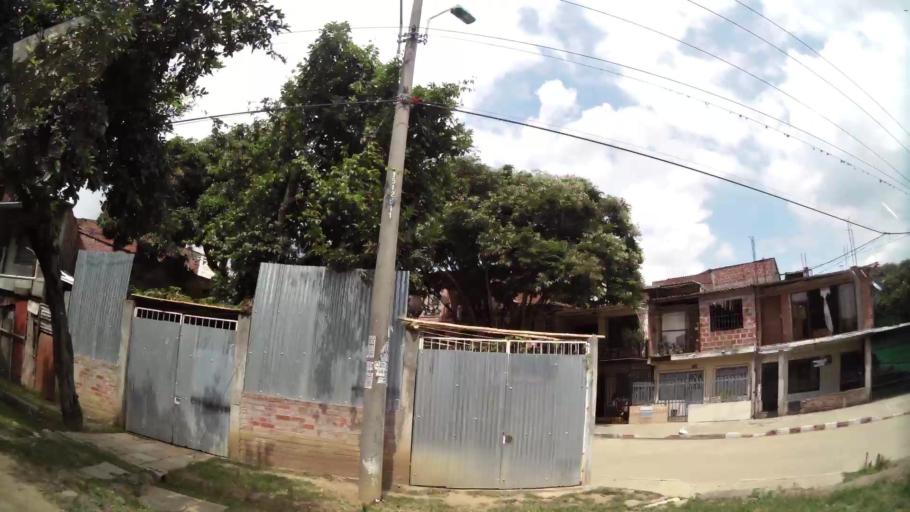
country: CO
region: Valle del Cauca
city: Cali
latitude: 3.4907
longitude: -76.4861
